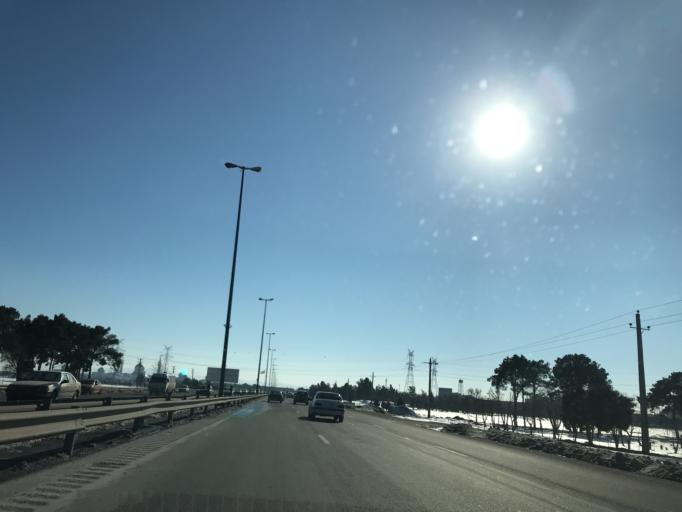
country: IR
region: Tehran
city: Rey
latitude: 35.5649
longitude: 51.3689
